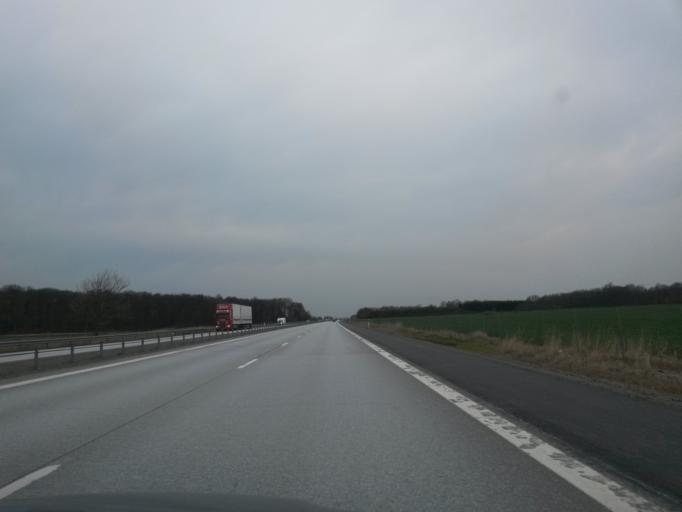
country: SE
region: Halland
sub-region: Falkenbergs Kommun
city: Falkenberg
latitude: 56.9520
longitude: 12.4676
